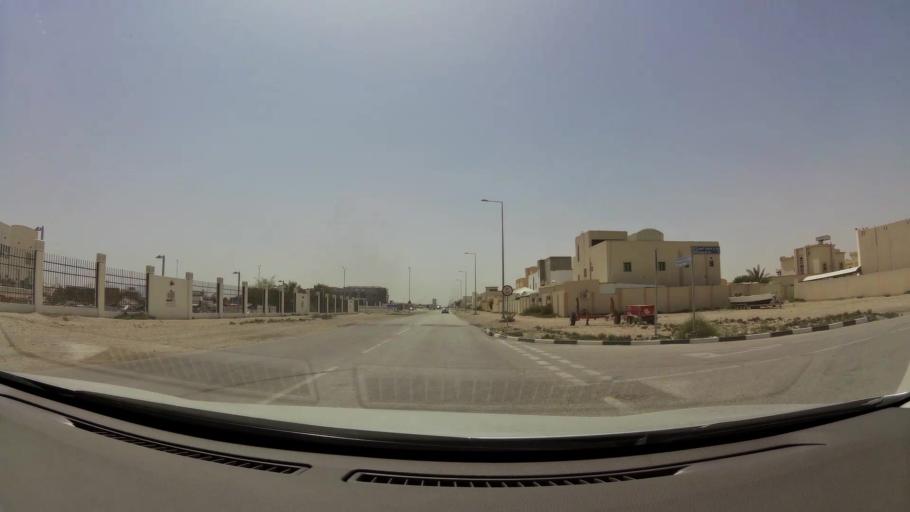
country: QA
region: Baladiyat Umm Salal
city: Umm Salal Muhammad
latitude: 25.3774
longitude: 51.4790
